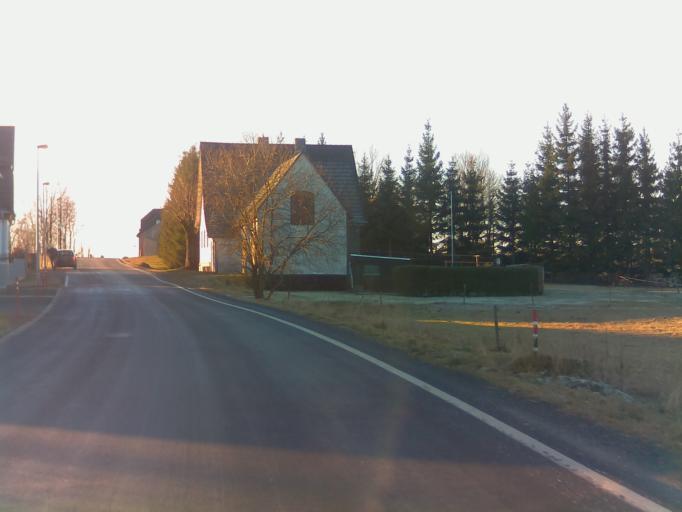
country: DE
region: Bavaria
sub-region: Upper Franconia
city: Tettau
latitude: 50.4402
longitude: 11.2399
